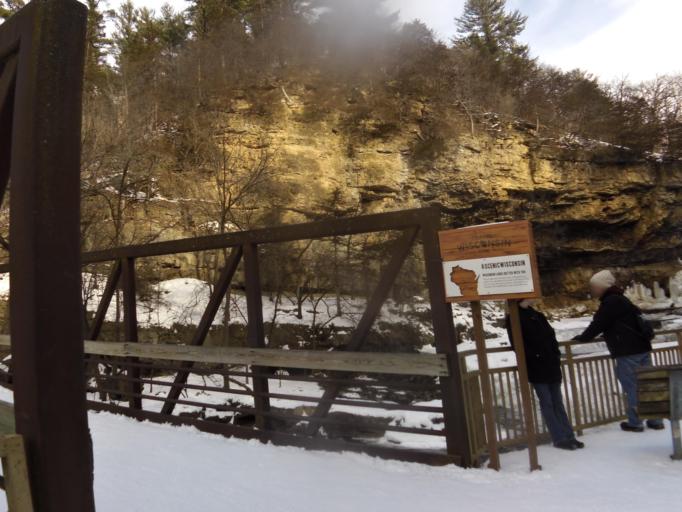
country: US
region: Wisconsin
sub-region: Saint Croix County
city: North Hudson
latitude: 45.0241
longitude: -92.6659
